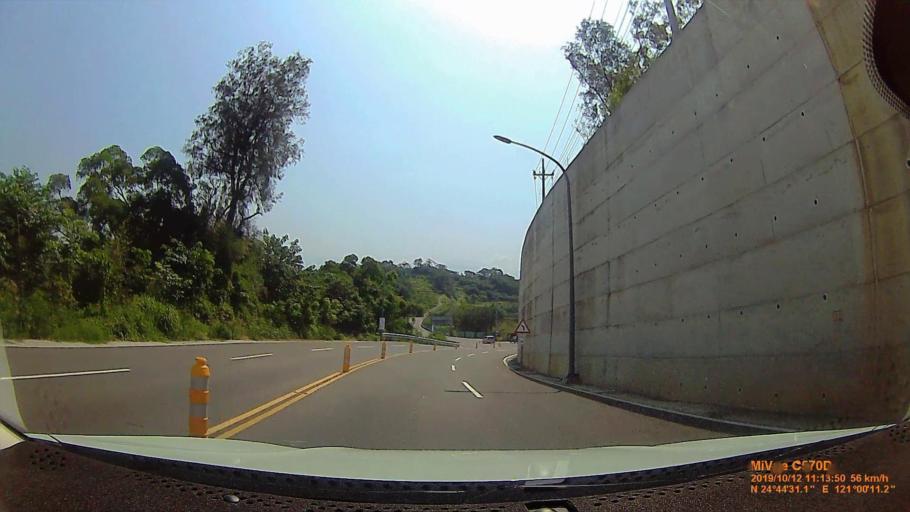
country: TW
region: Taiwan
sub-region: Hsinchu
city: Hsinchu
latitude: 24.7417
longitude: 121.0032
